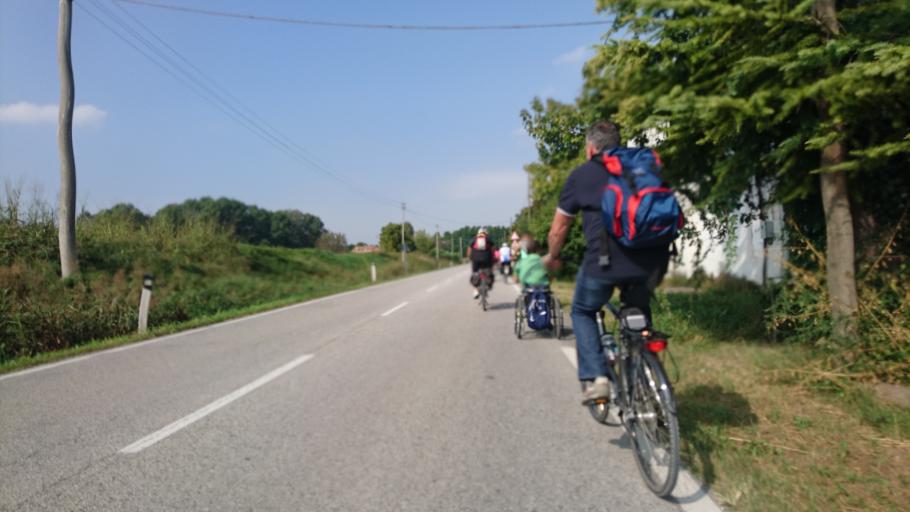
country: IT
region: Veneto
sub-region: Provincia di Padova
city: San Giorgio in Bosco
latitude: 45.5860
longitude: 11.7680
